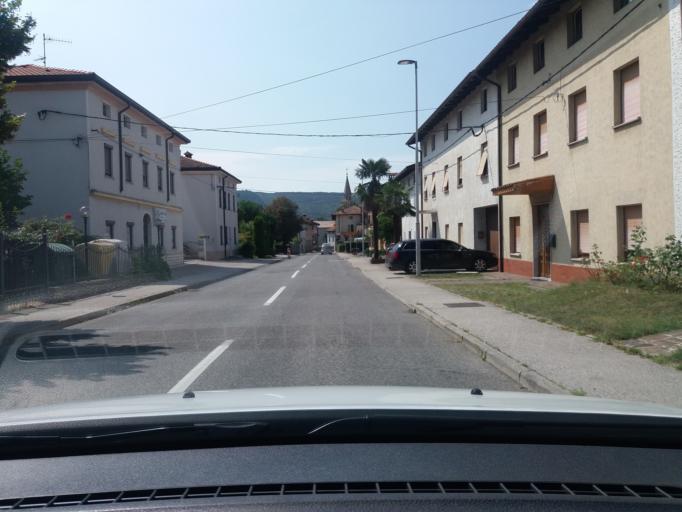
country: SI
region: Miren-Kostanjevica
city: Miren
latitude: 45.8972
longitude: 13.6084
